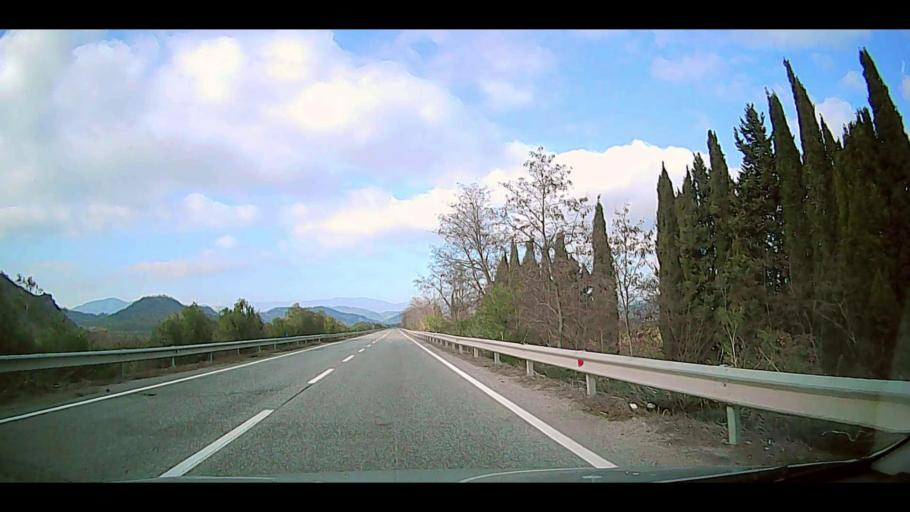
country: IT
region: Calabria
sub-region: Provincia di Crotone
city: Rocca di Neto
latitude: 39.1694
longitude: 16.9788
